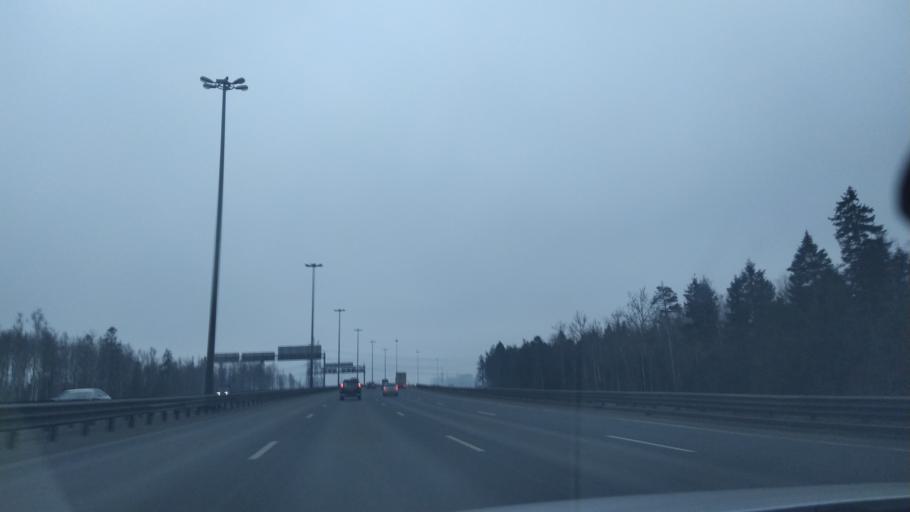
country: RU
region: St.-Petersburg
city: Krasnogvargeisky
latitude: 59.9355
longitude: 30.5383
